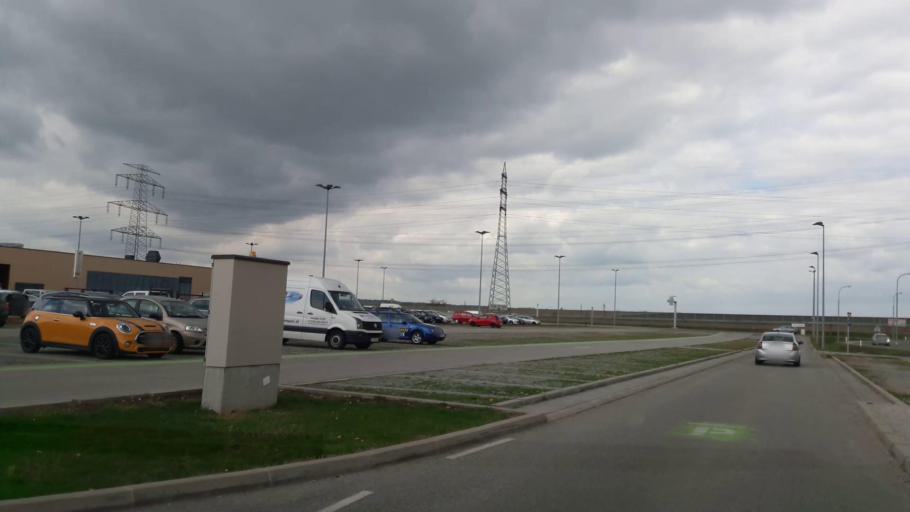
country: AT
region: Lower Austria
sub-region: Politischer Bezirk Mistelbach
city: Grossebersdorf
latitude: 48.3442
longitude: 16.4646
